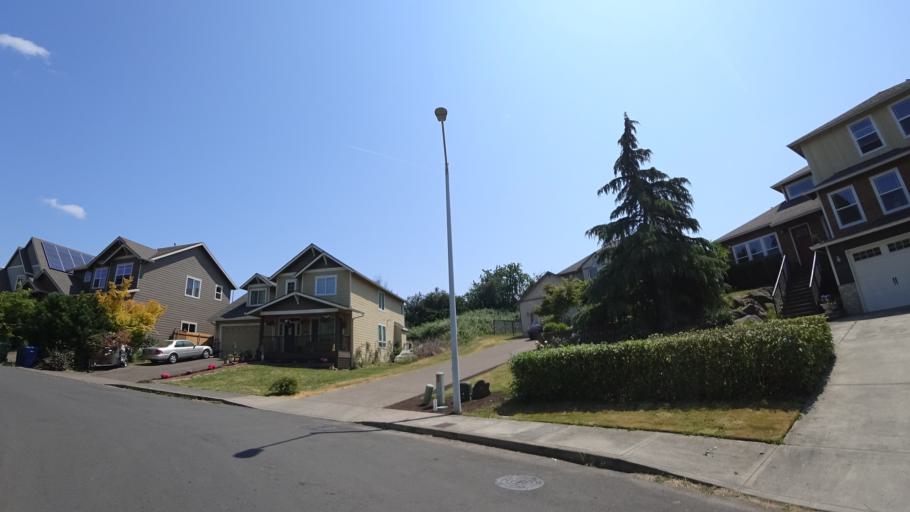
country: US
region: Oregon
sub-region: Clackamas County
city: Clackamas
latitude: 45.4436
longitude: -122.5714
